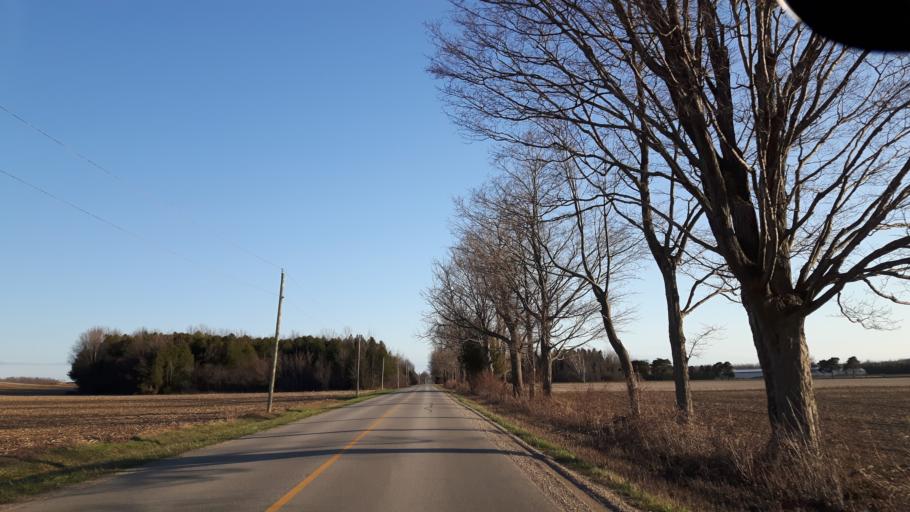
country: CA
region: Ontario
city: Goderich
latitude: 43.6922
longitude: -81.6848
